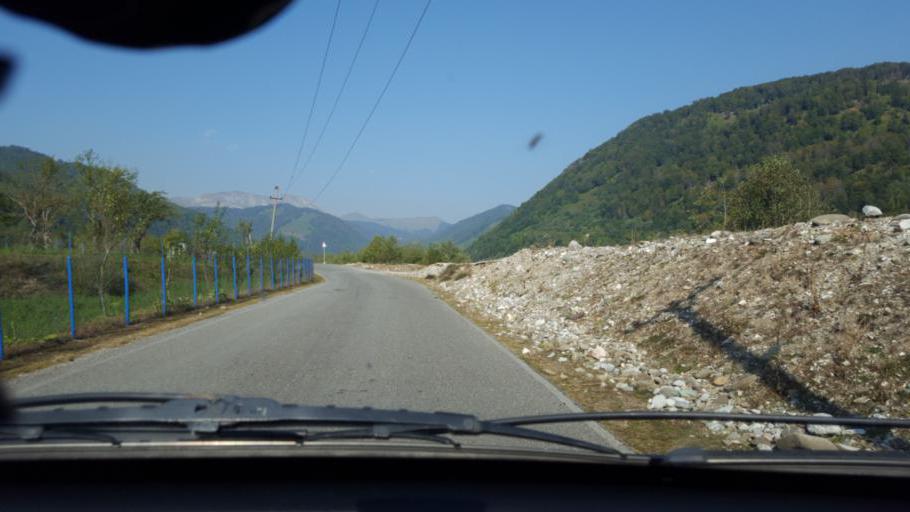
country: ME
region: Andrijevica
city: Andrijevica
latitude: 42.5890
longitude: 19.7002
